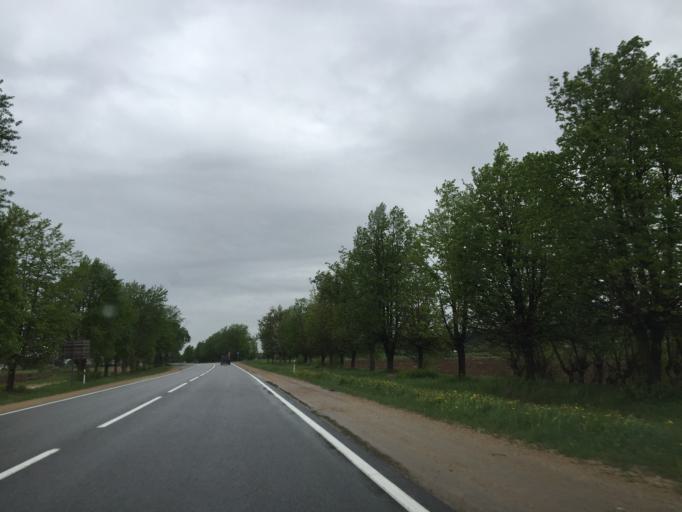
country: LV
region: Ogre
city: Ogre
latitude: 56.7873
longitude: 24.6423
